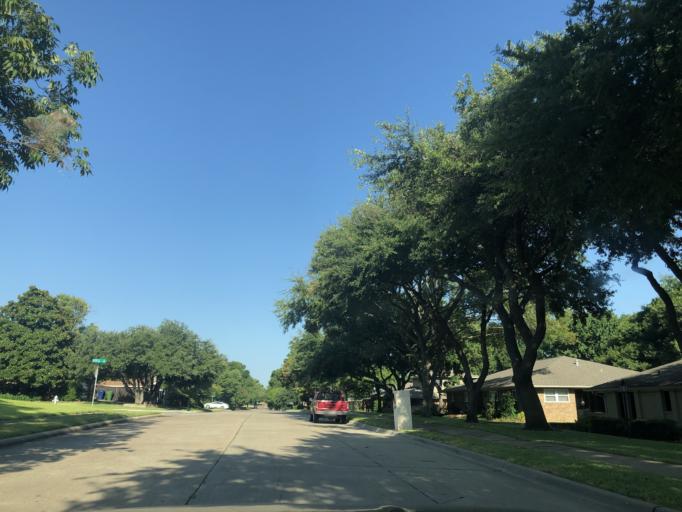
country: US
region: Texas
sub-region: Dallas County
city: Garland
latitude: 32.8710
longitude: -96.6390
